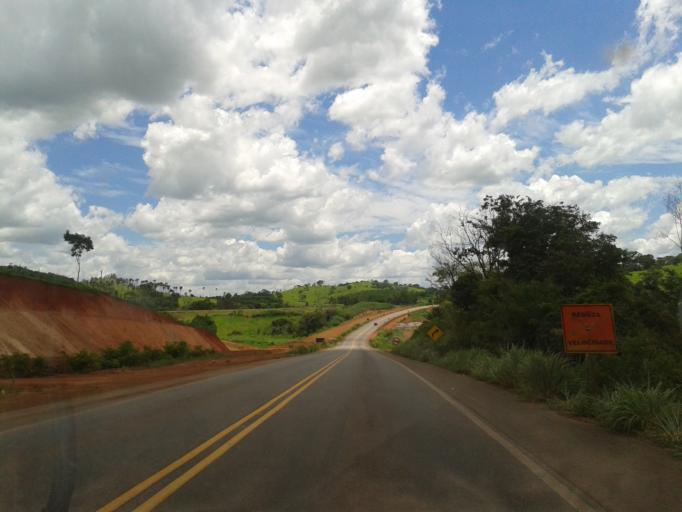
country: BR
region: Goias
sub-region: Petrolina De Goias
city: Petrolina de Goias
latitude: -16.2053
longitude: -49.3116
